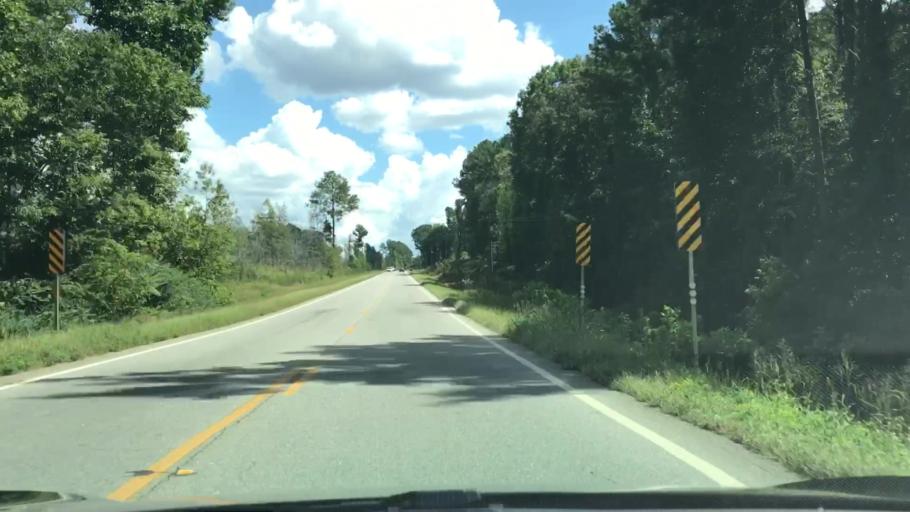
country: US
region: Georgia
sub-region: Greene County
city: Greensboro
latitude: 33.6103
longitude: -83.2054
